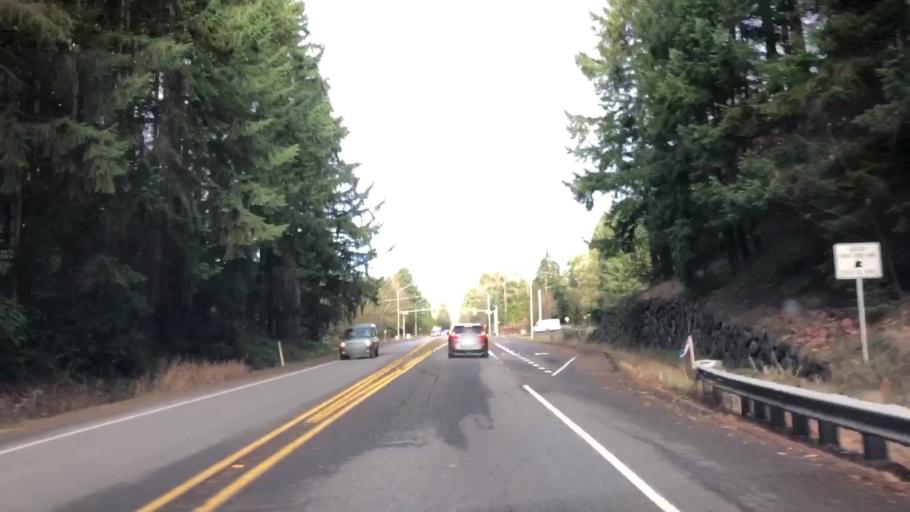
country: US
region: Washington
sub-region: Kitsap County
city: Bainbridge Island
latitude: 47.6781
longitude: -122.5379
